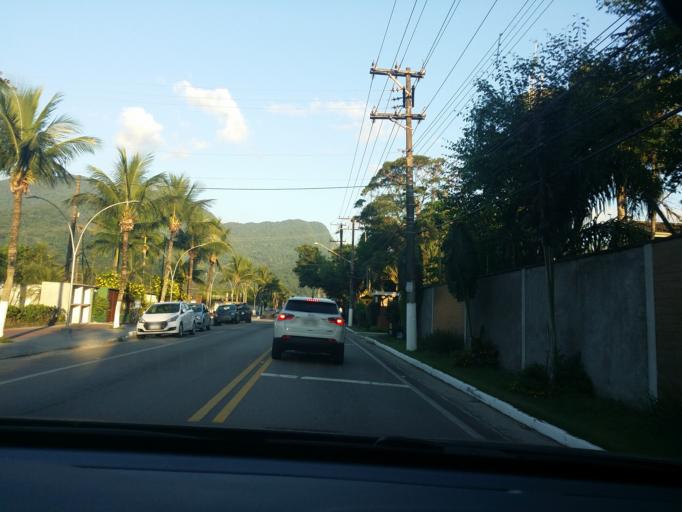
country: BR
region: Sao Paulo
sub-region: Sao Sebastiao
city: Sao Sebastiao
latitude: -23.7901
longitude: -45.5706
